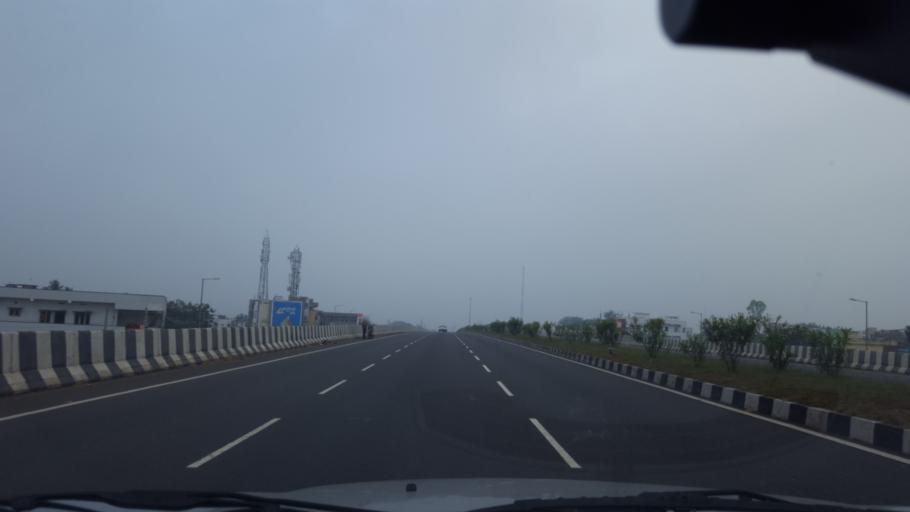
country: IN
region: Andhra Pradesh
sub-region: Prakasam
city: Ongole
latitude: 15.6190
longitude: 80.0226
